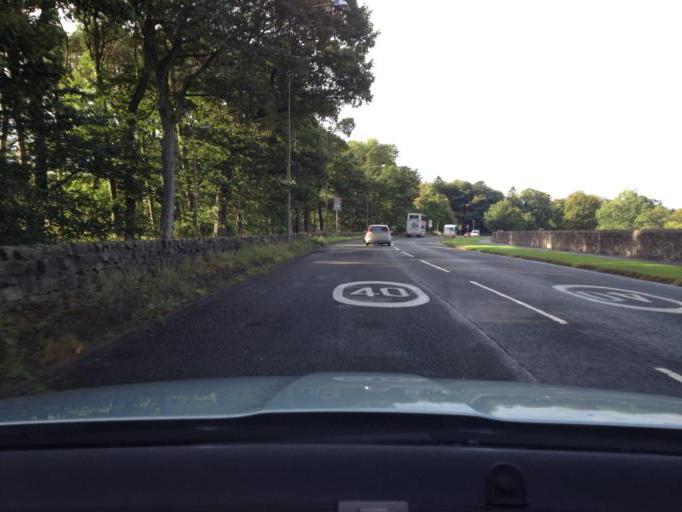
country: GB
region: Scotland
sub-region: West Lothian
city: West Calder
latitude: 55.8652
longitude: -3.5381
